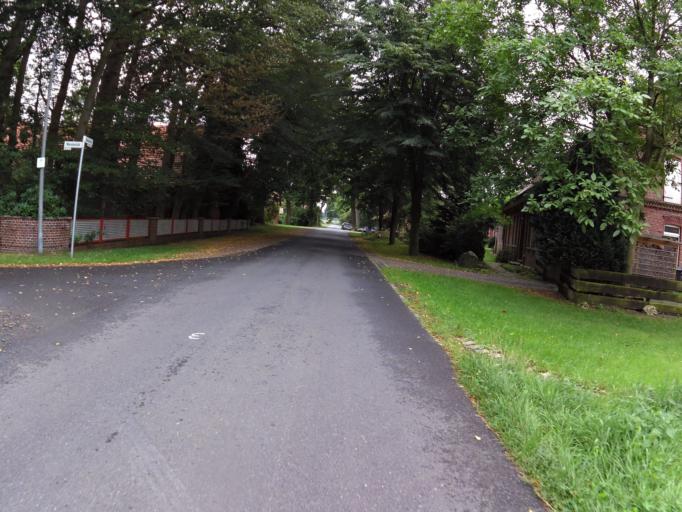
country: DE
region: Lower Saxony
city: Helvesiek
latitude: 53.1977
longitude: 9.4634
